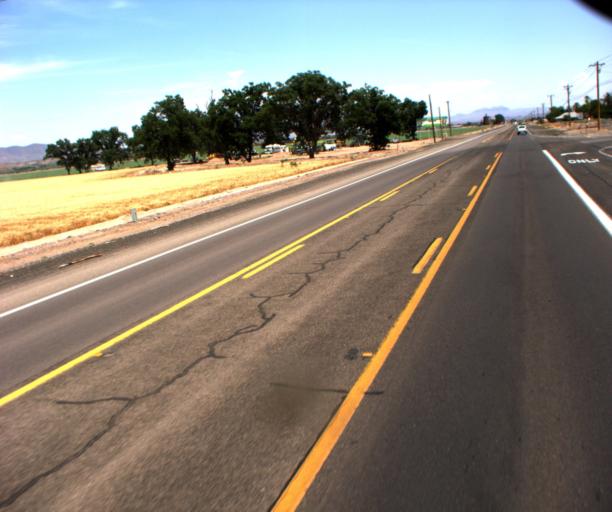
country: US
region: Arizona
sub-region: Graham County
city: Safford
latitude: 32.8166
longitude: -109.6582
